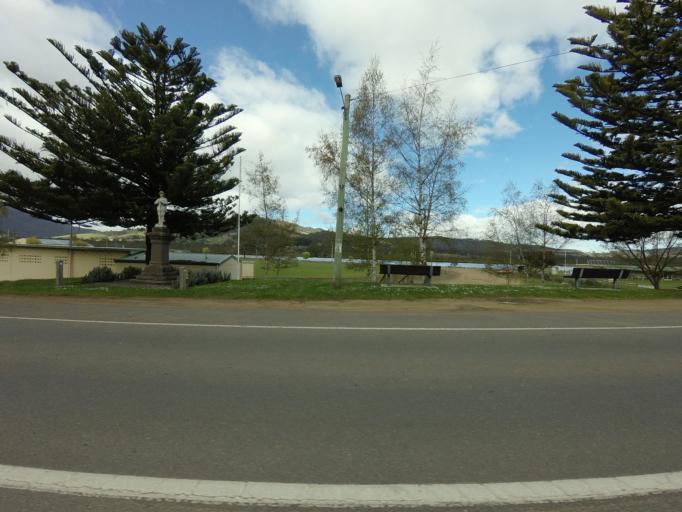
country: AU
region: Tasmania
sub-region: Huon Valley
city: Franklin
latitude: -43.0892
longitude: 147.0108
